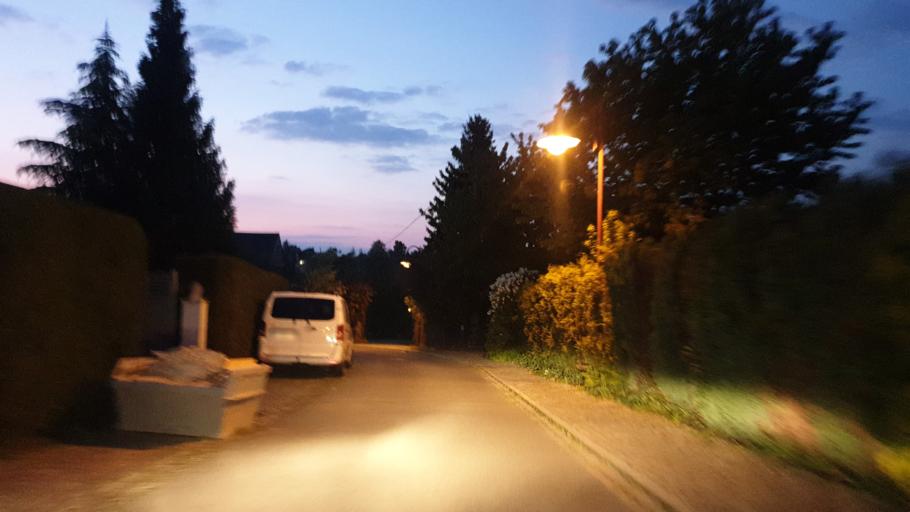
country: DE
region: Saxony
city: Lugau
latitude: 50.7193
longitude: 12.7511
